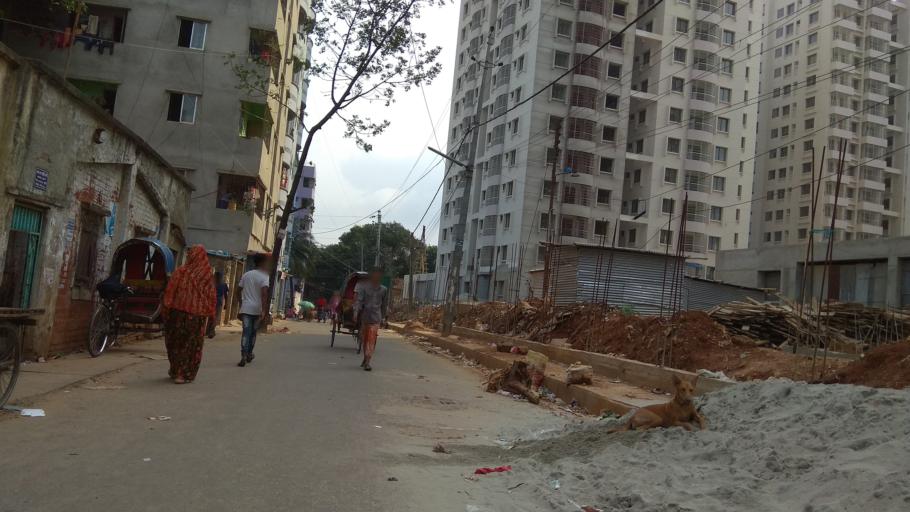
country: BD
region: Dhaka
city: Azimpur
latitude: 23.8139
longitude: 90.3595
